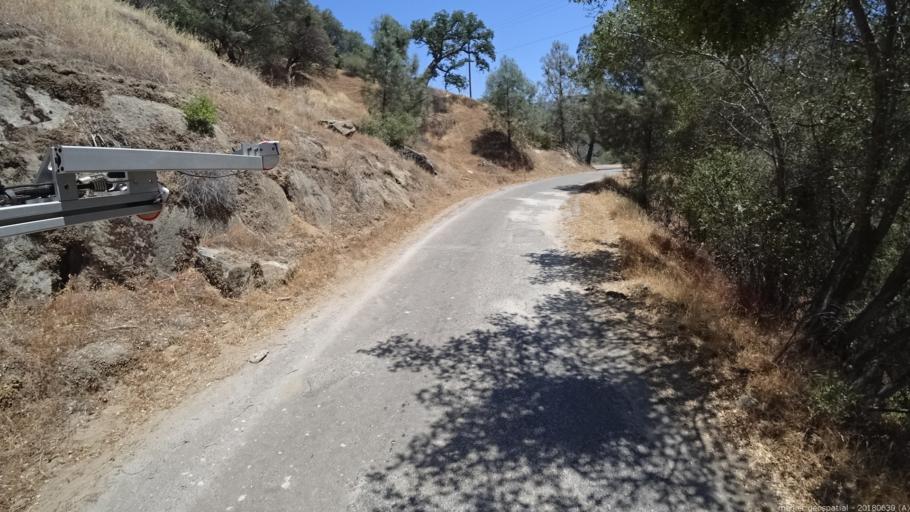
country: US
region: California
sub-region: Fresno County
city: Auberry
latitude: 37.1620
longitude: -119.4079
